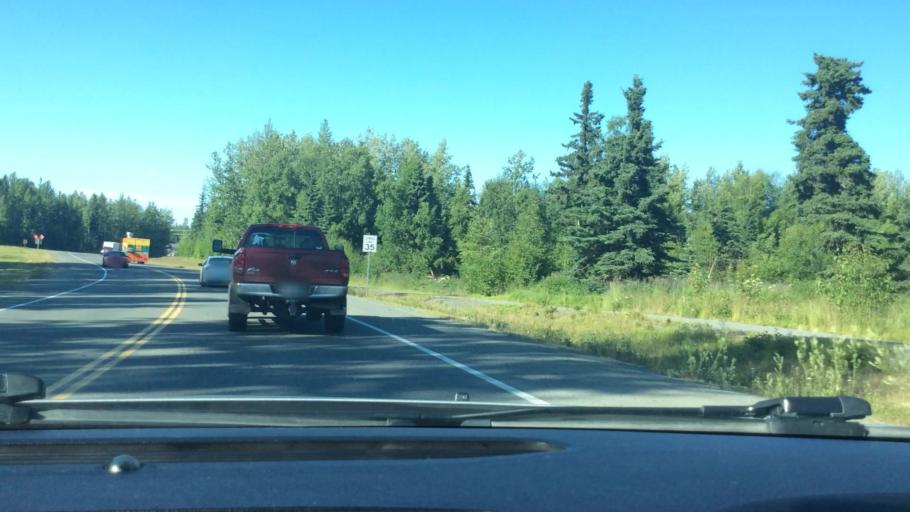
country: US
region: Alaska
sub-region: Anchorage Municipality
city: Elmendorf Air Force Base
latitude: 61.2422
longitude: -149.7062
